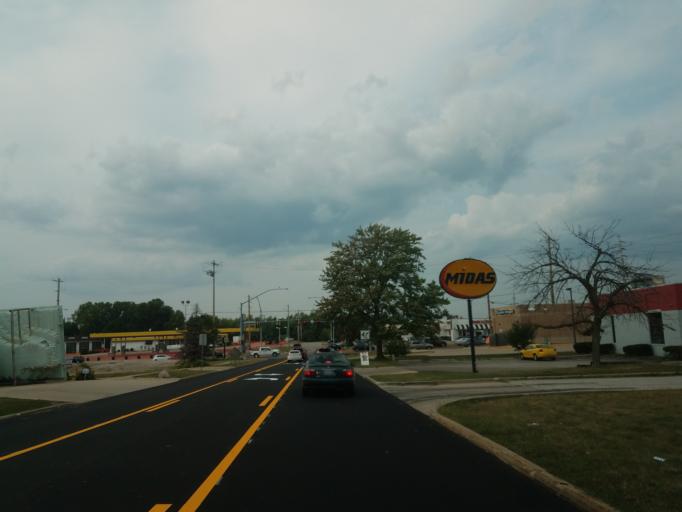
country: US
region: Illinois
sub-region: McLean County
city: Normal
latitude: 40.5017
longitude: -88.9543
